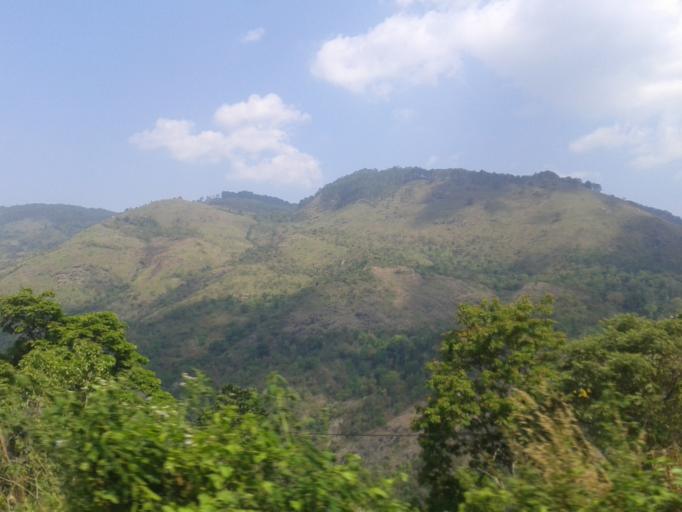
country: IN
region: Tamil Nadu
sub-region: Dindigul
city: Ayakudi
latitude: 10.3435
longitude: 77.5748
